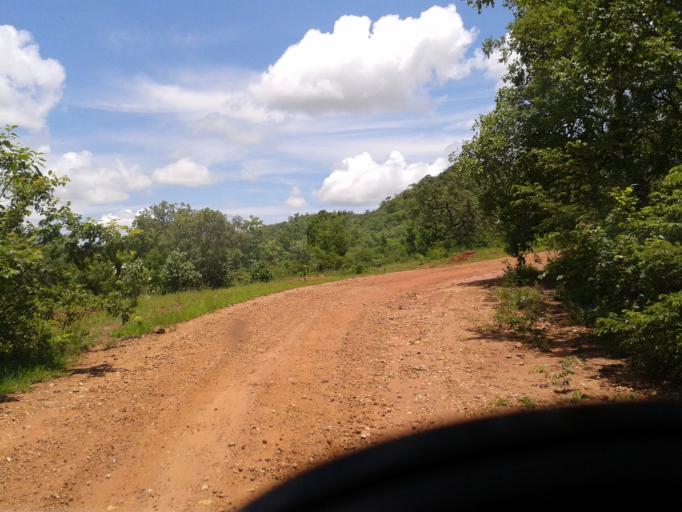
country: BR
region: Minas Gerais
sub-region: Santa Vitoria
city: Santa Vitoria
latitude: -18.9856
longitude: -49.8979
